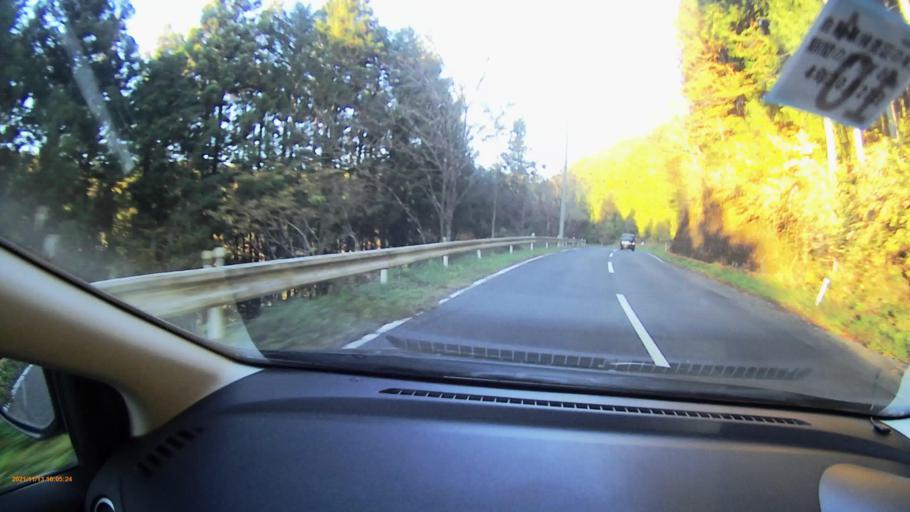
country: JP
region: Gifu
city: Nakatsugawa
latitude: 35.5988
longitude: 137.4717
